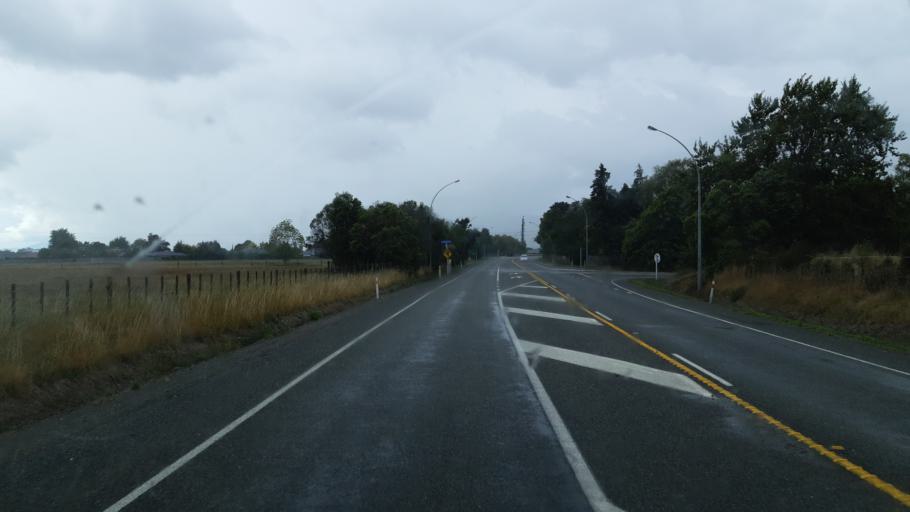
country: NZ
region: Tasman
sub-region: Tasman District
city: Brightwater
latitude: -41.3778
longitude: 173.0985
